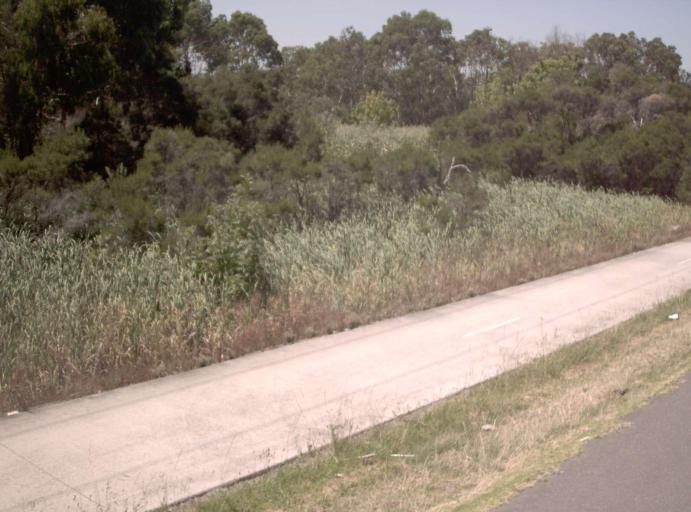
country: AU
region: Victoria
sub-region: Monash
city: Mulgrave
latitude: -37.9242
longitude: 145.2044
